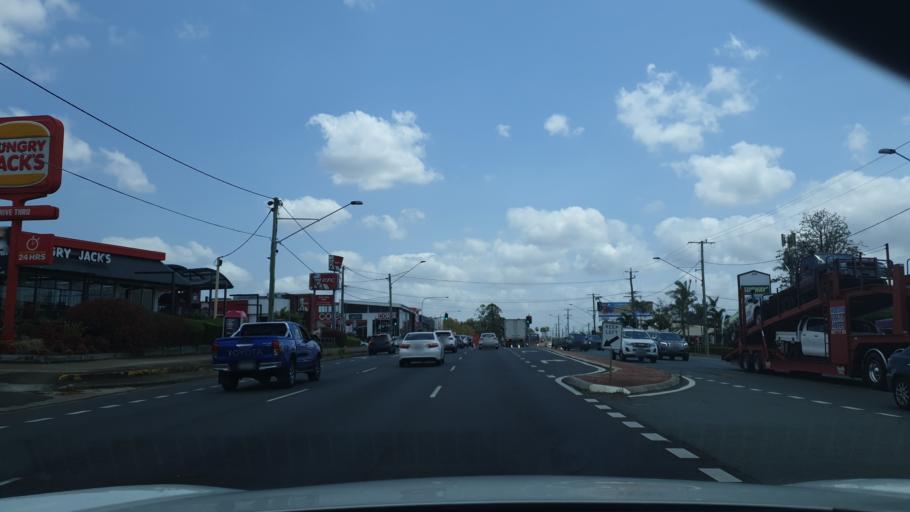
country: AU
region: Queensland
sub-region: Brisbane
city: Gordon Park
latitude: -27.4049
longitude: 153.0320
